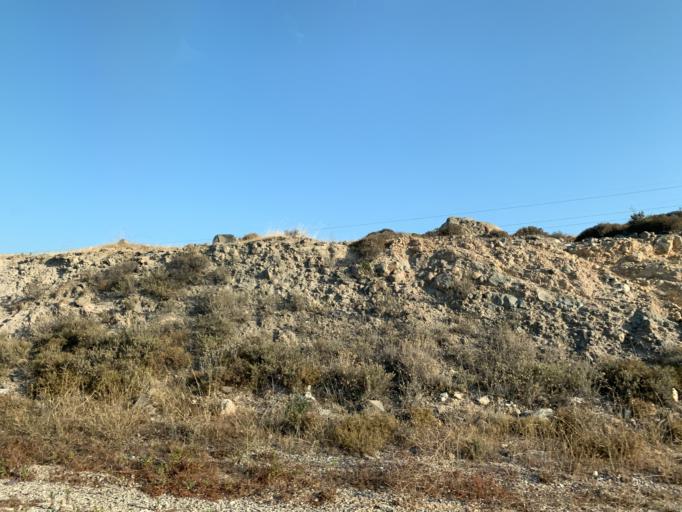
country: TR
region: Izmir
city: Alacati
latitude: 38.2775
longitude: 26.4248
